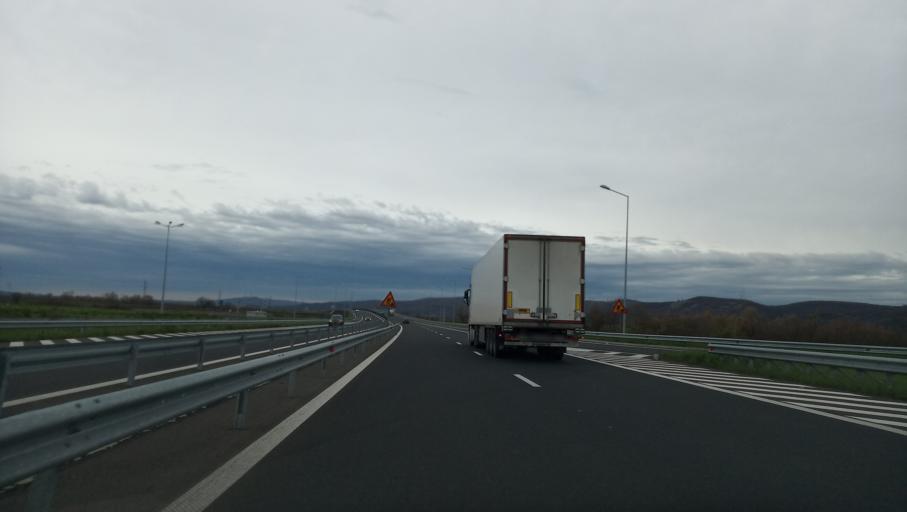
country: RO
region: Hunedoara
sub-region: Comuna Ilia
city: Ilia
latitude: 45.9480
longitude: 22.6525
